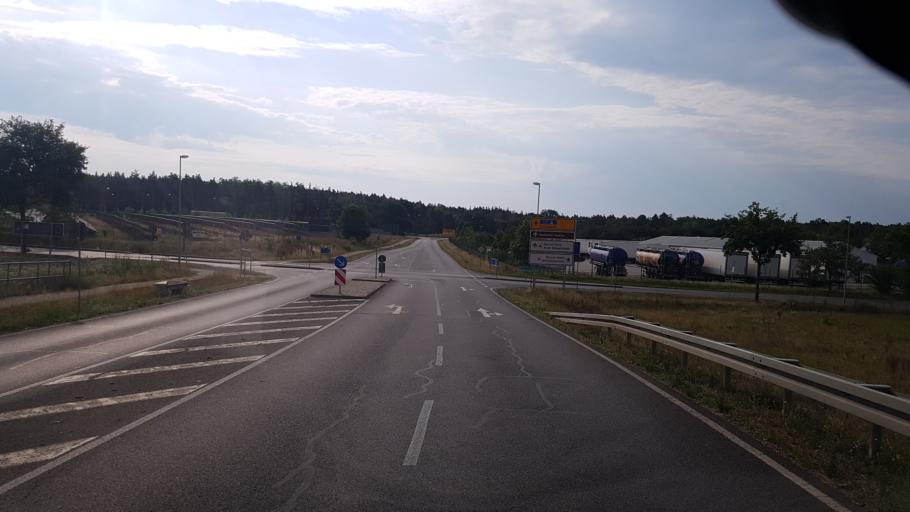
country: DE
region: Brandenburg
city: Baruth
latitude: 52.0641
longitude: 13.5114
